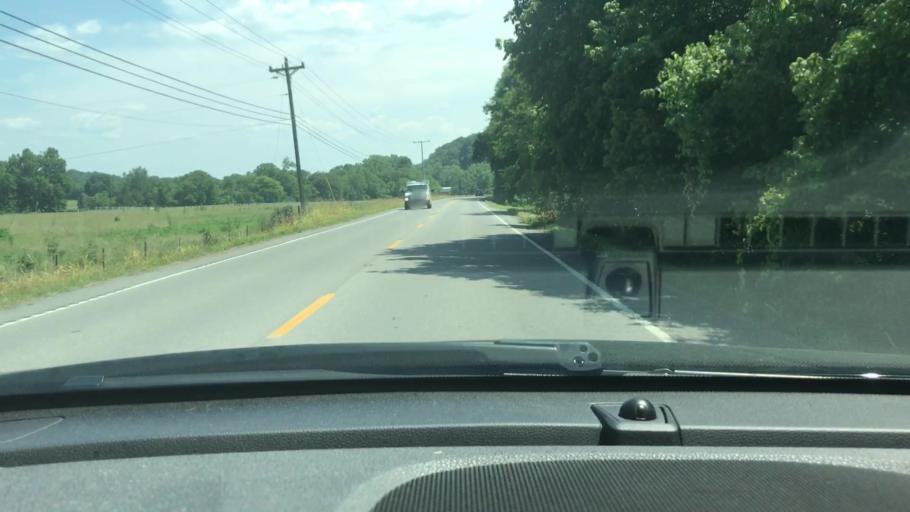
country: US
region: Tennessee
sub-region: Sumner County
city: Shackle Island
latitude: 36.4005
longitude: -86.6304
